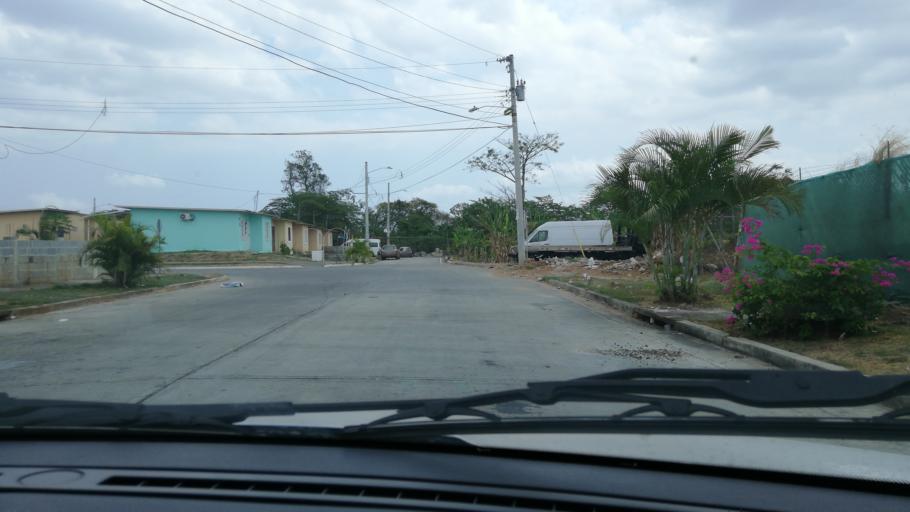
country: PA
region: Panama
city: Tocumen
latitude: 9.0754
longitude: -79.3521
